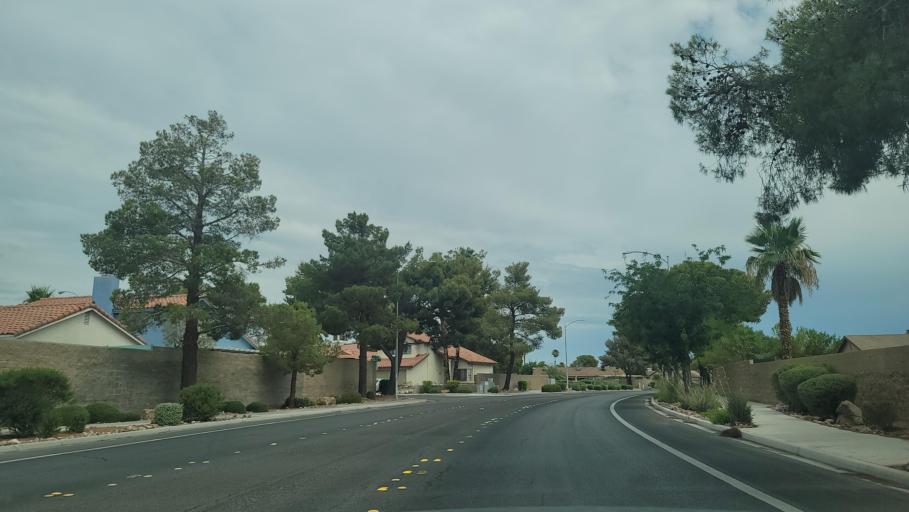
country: US
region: Nevada
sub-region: Clark County
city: Spring Valley
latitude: 36.1046
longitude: -115.2493
